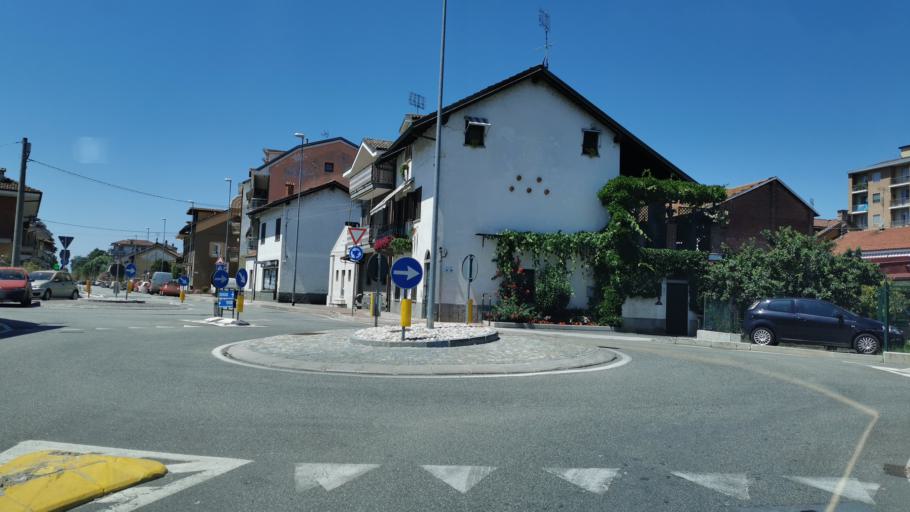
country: IT
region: Piedmont
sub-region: Provincia di Torino
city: Brandizzo
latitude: 45.1771
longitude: 7.8370
